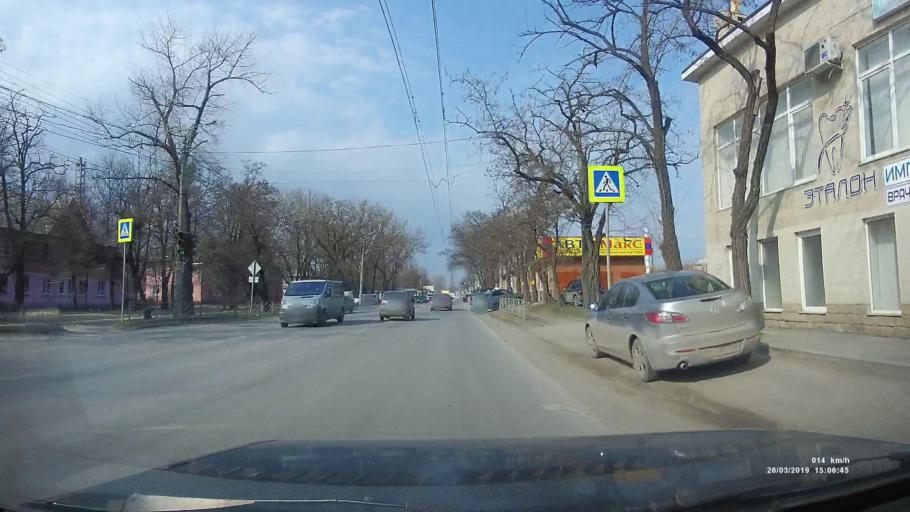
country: RU
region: Rostov
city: Taganrog
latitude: 47.2365
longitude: 38.8850
